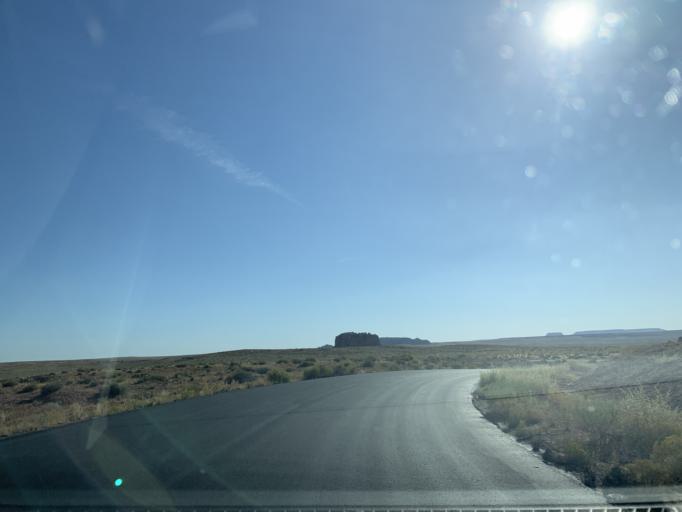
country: US
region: Utah
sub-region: Emery County
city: Ferron
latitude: 38.5722
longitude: -110.7100
